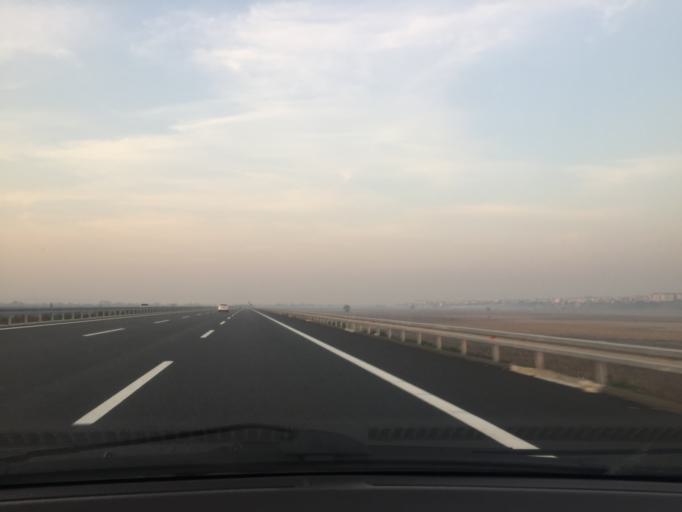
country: TR
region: Bursa
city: Karacabey
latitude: 40.2167
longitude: 28.3950
